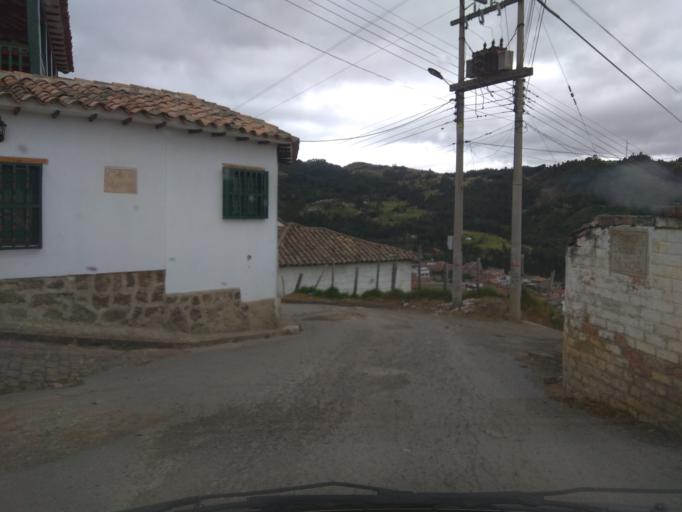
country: CO
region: Boyaca
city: Mongui
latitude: 5.7247
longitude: -72.8477
